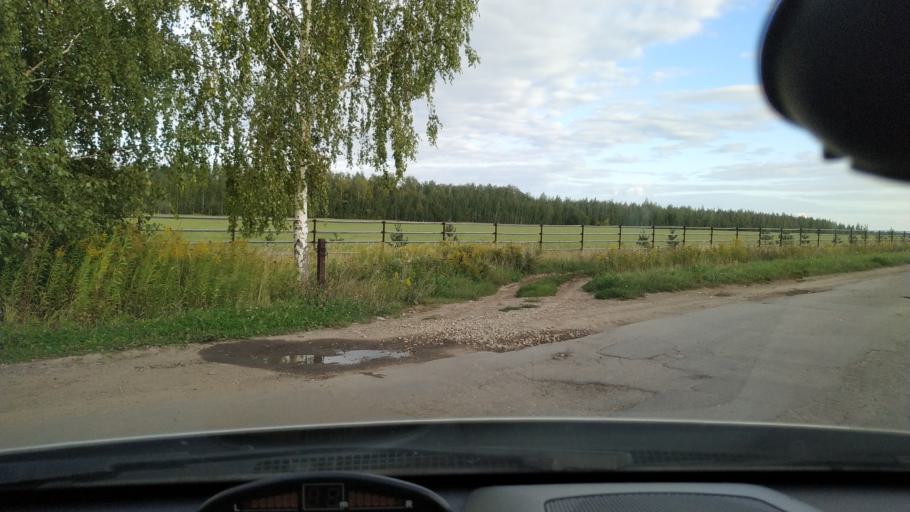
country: RU
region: Rjazan
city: Polyany
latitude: 54.5788
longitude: 39.8603
